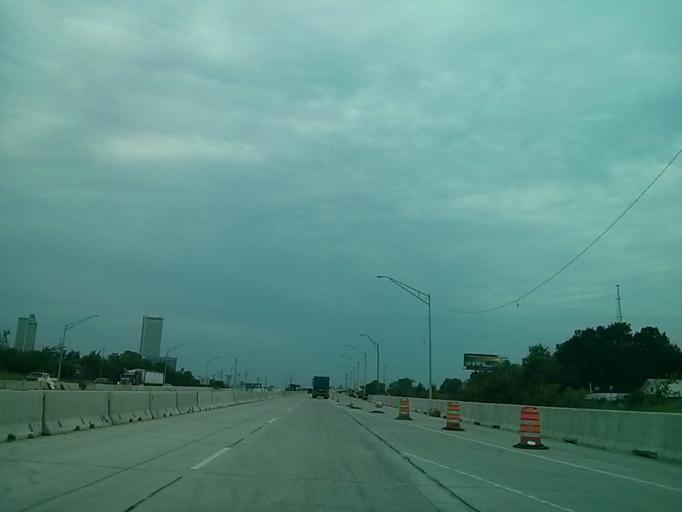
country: US
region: Oklahoma
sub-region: Tulsa County
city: Tulsa
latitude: 36.1593
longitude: -95.9708
